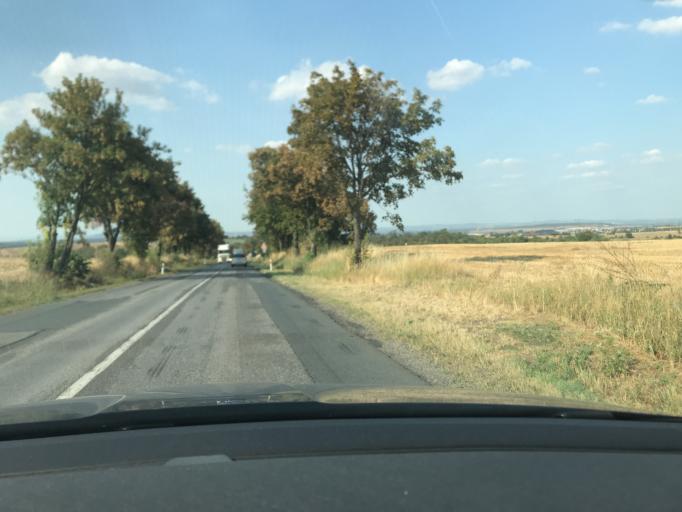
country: CZ
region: Central Bohemia
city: Kralupy nad Vltavou
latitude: 50.2129
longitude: 14.3165
